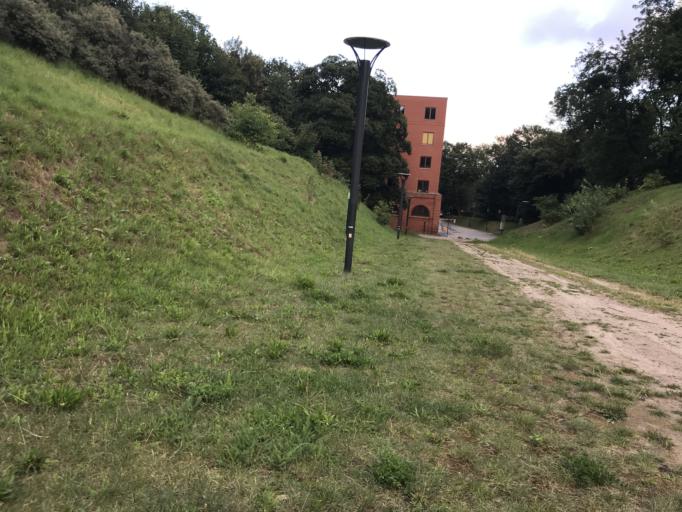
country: PL
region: Pomeranian Voivodeship
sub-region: Gdansk
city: Gdansk
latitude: 54.3551
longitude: 18.6395
